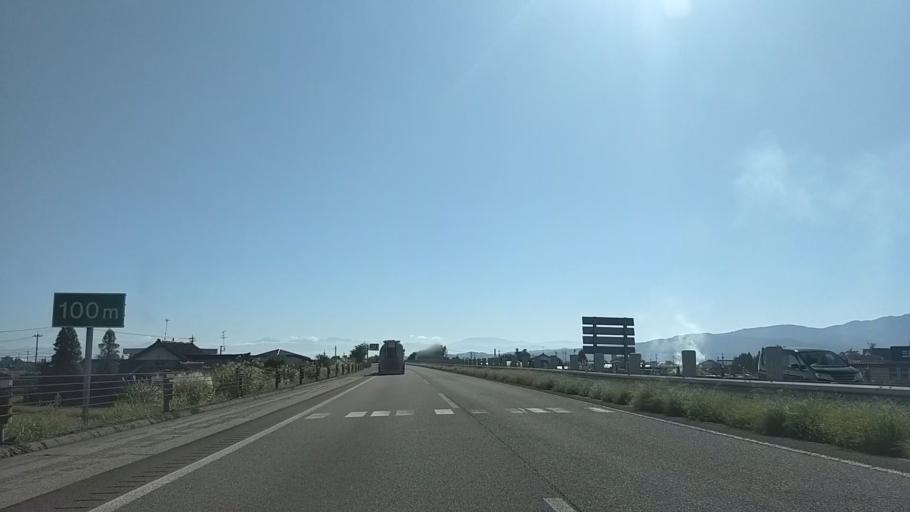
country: JP
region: Toyama
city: Nanto-shi
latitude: 36.6236
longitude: 136.9366
